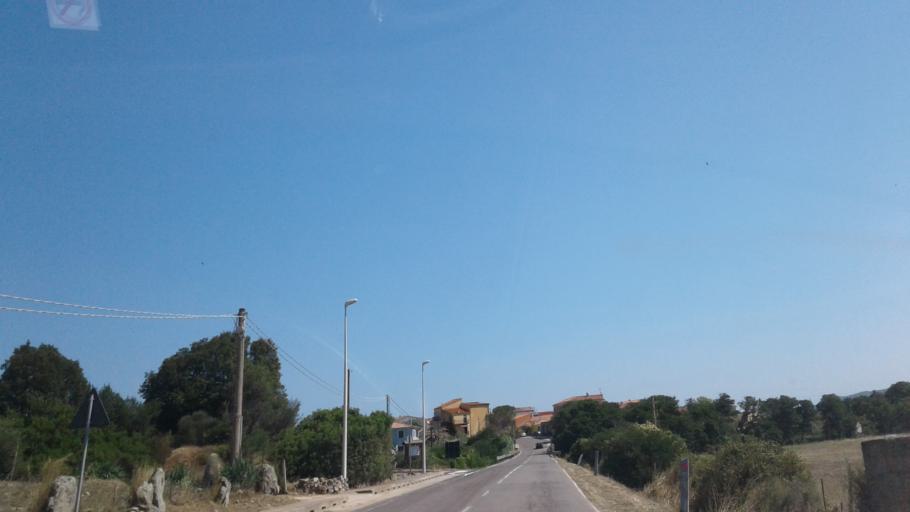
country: IT
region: Sardinia
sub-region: Provincia di Olbia-Tempio
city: Luogosanto
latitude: 41.1058
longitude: 9.2596
